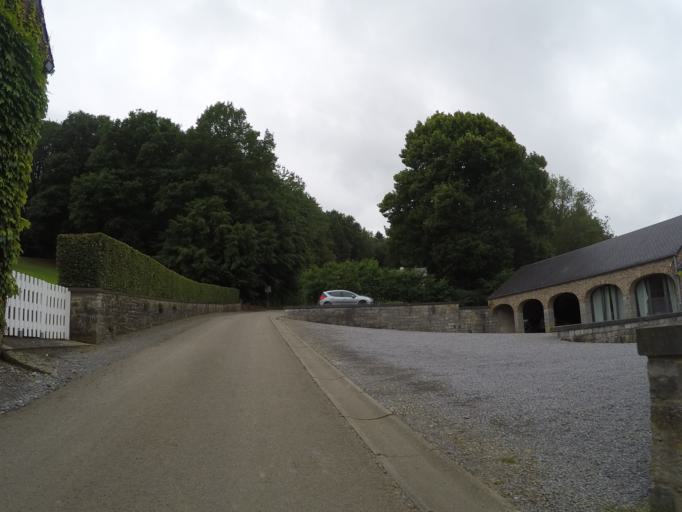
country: BE
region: Wallonia
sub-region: Province de Namur
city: Yvoir
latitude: 50.3250
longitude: 4.9262
